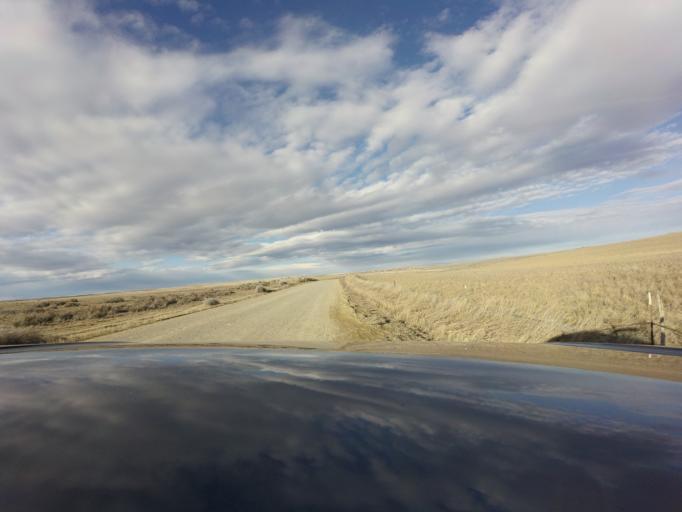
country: US
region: Montana
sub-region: Yellowstone County
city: Laurel
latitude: 45.8621
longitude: -108.8814
